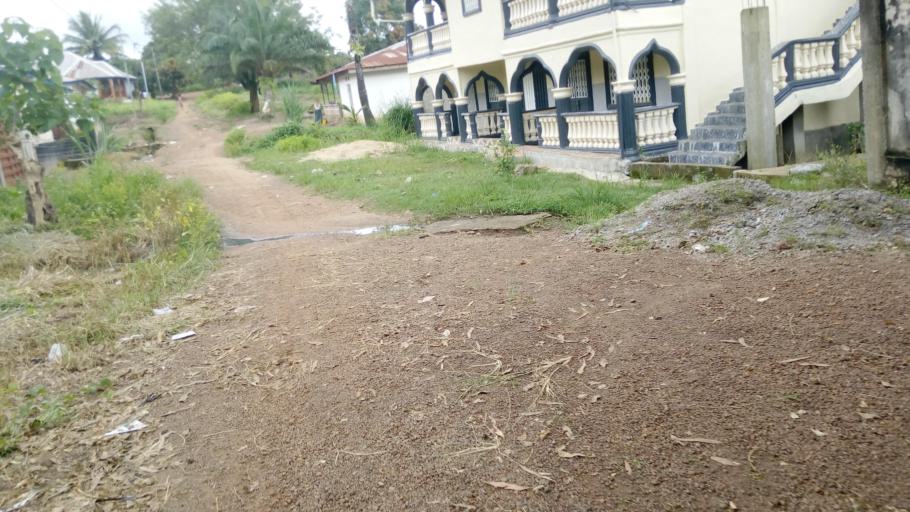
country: SL
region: Northern Province
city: Makeni
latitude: 8.8876
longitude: -12.0291
